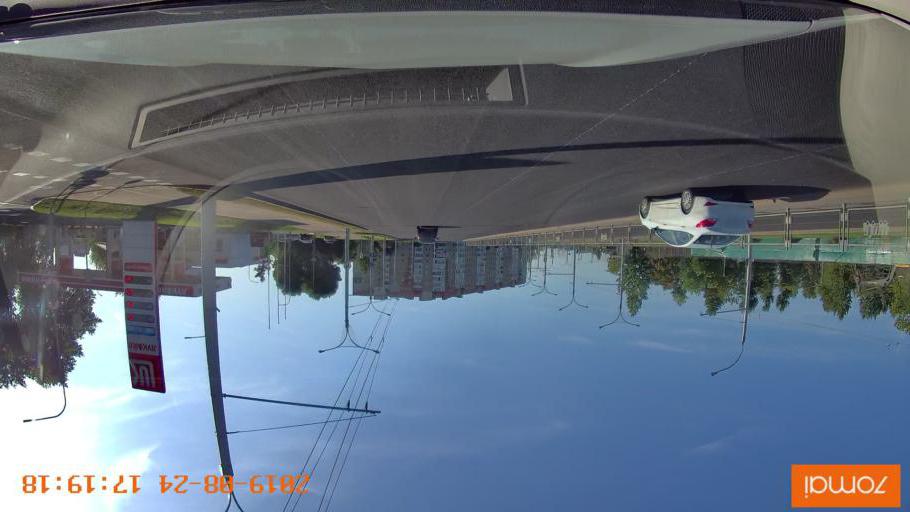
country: BY
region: Minsk
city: Vyaliki Trastsyanets
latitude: 53.8629
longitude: 27.6419
